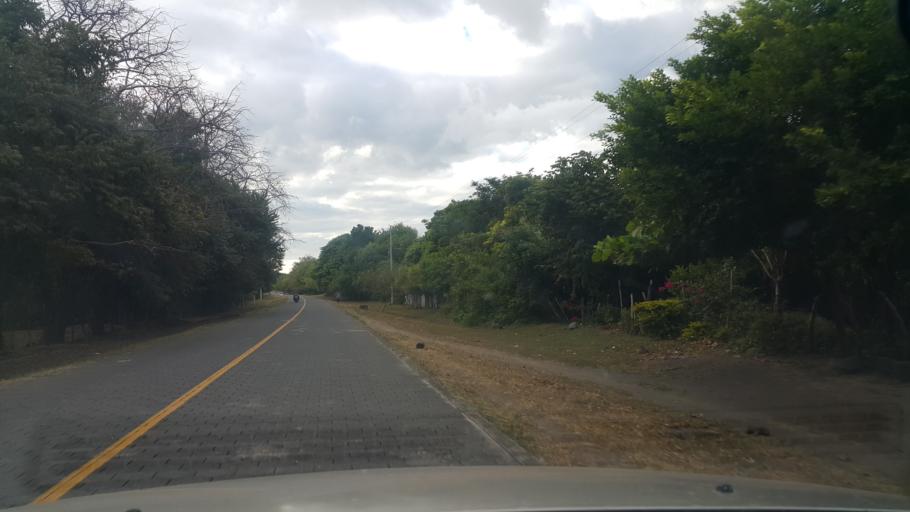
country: NI
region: Rivas
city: Moyogalpa
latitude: 11.4929
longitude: -85.6701
